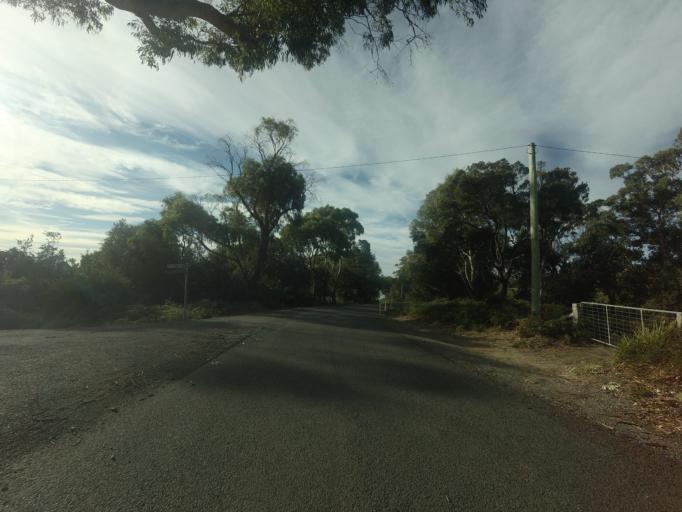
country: AU
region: Tasmania
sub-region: Sorell
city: Sorell
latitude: -42.9657
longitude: 147.8310
